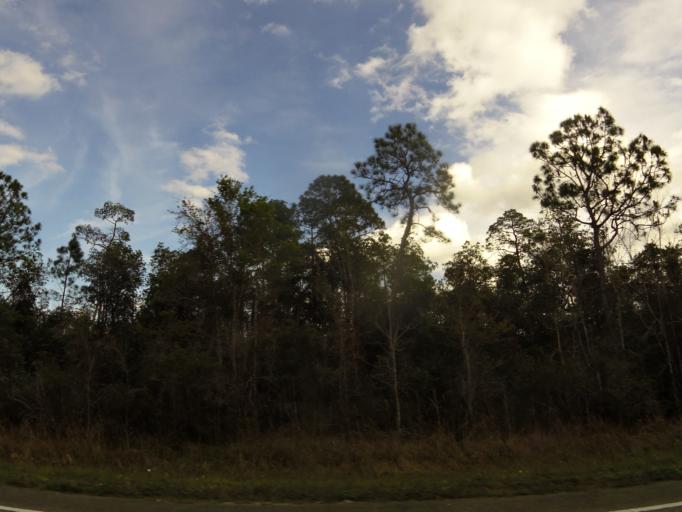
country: US
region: Florida
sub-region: Volusia County
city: De Leon Springs
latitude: 29.2446
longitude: -81.3255
